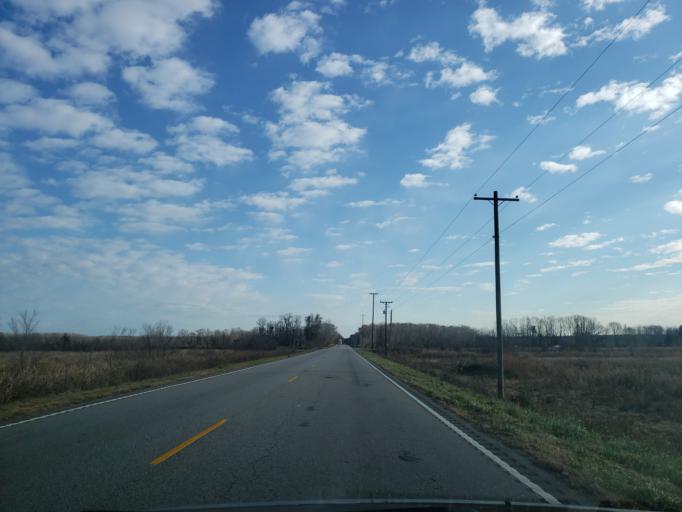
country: US
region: Georgia
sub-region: Chatham County
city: Port Wentworth
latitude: 32.1724
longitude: -81.0988
